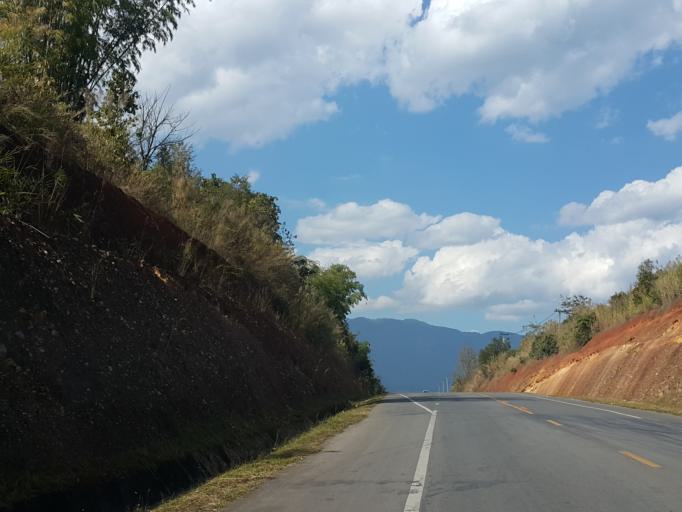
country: TH
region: Chiang Mai
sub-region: Amphoe Chiang Dao
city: Chiang Dao
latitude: 19.3619
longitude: 98.9525
